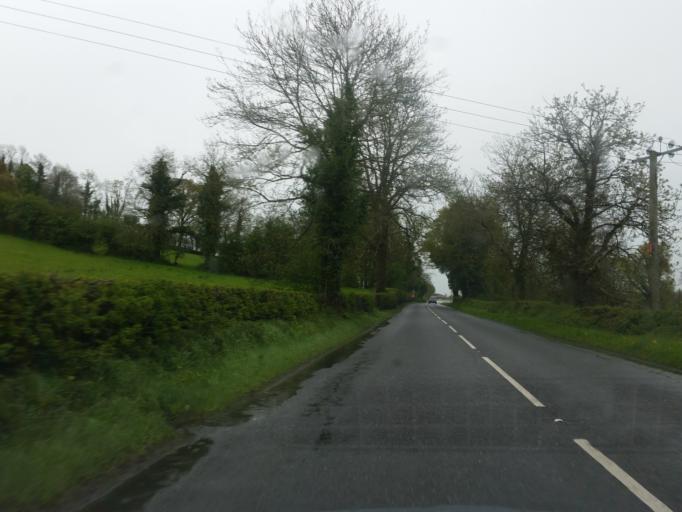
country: GB
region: Northern Ireland
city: Lisnaskea
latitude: 54.2249
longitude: -7.4139
